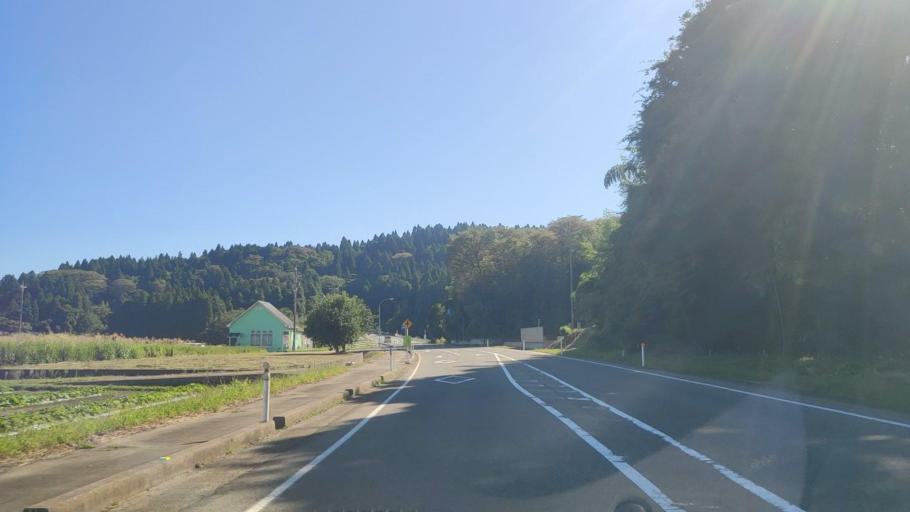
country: JP
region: Ishikawa
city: Nanao
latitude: 37.3877
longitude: 137.2330
